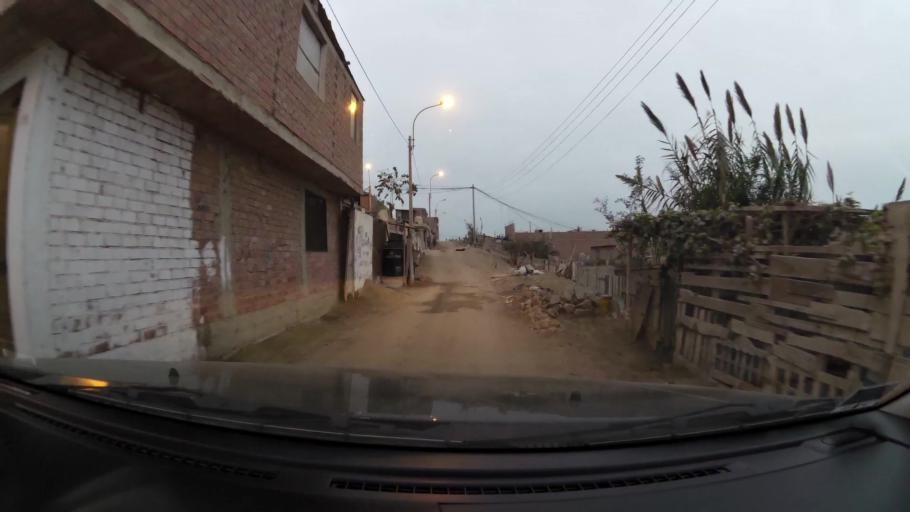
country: PE
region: Lima
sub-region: Lima
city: Surco
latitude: -12.1934
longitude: -77.0251
